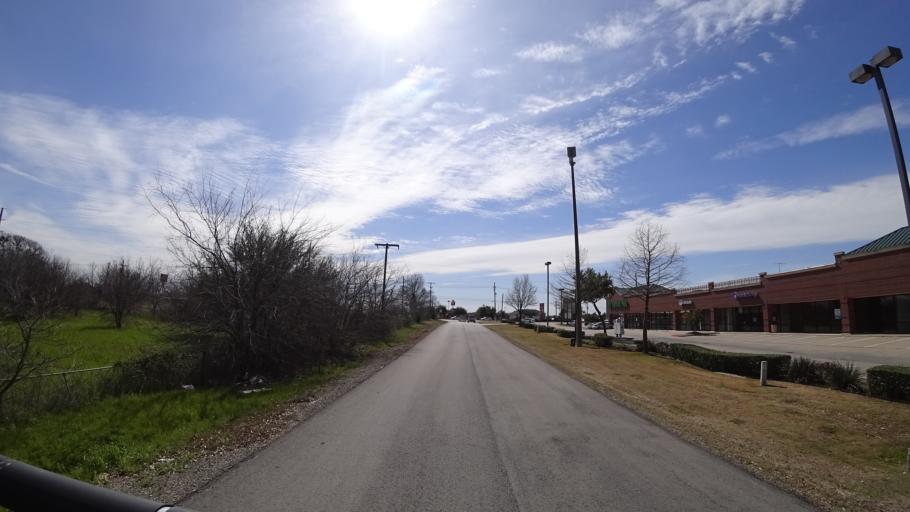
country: US
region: Texas
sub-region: Denton County
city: Lewisville
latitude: 33.0056
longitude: -96.9854
